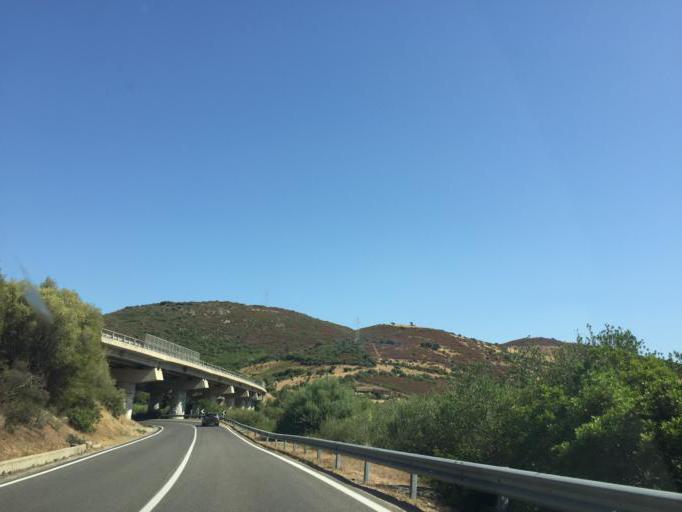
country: IT
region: Sardinia
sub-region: Provincia di Olbia-Tempio
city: San Teodoro
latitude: 40.7313
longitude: 9.6494
